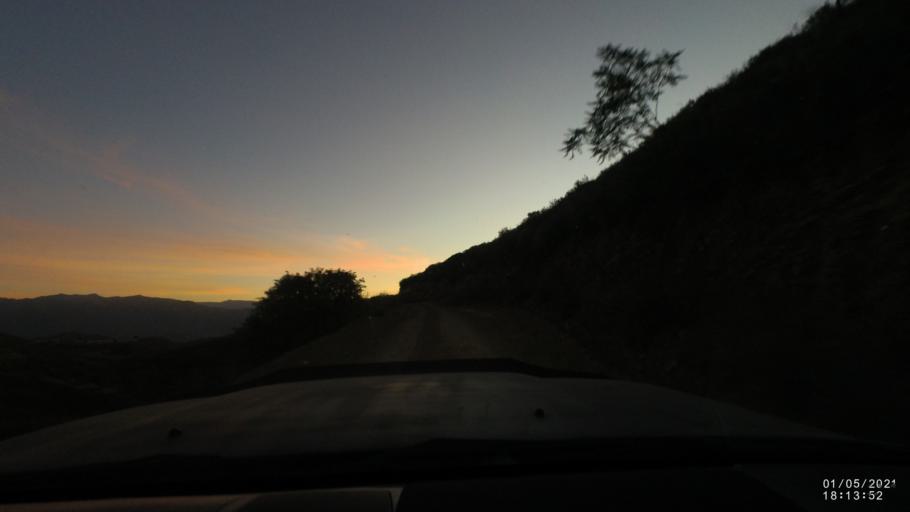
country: BO
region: Cochabamba
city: Capinota
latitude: -17.6754
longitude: -66.2092
